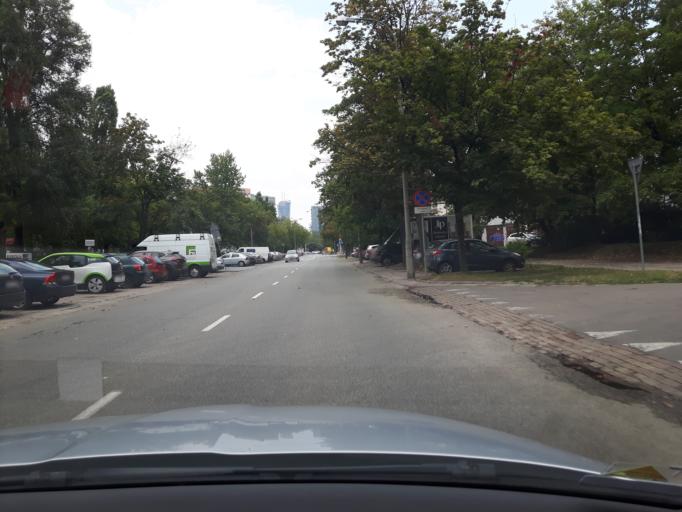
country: PL
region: Masovian Voivodeship
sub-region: Warszawa
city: Ochota
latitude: 52.2167
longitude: 20.9712
